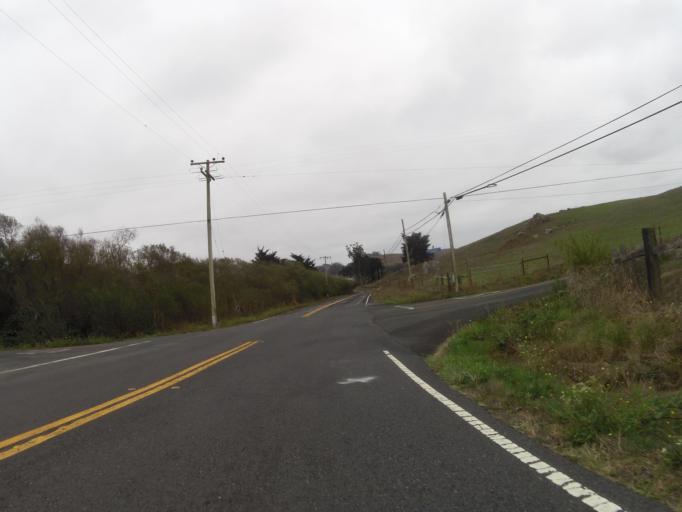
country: US
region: California
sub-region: Sonoma County
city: Occidental
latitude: 38.2765
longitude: -122.9000
